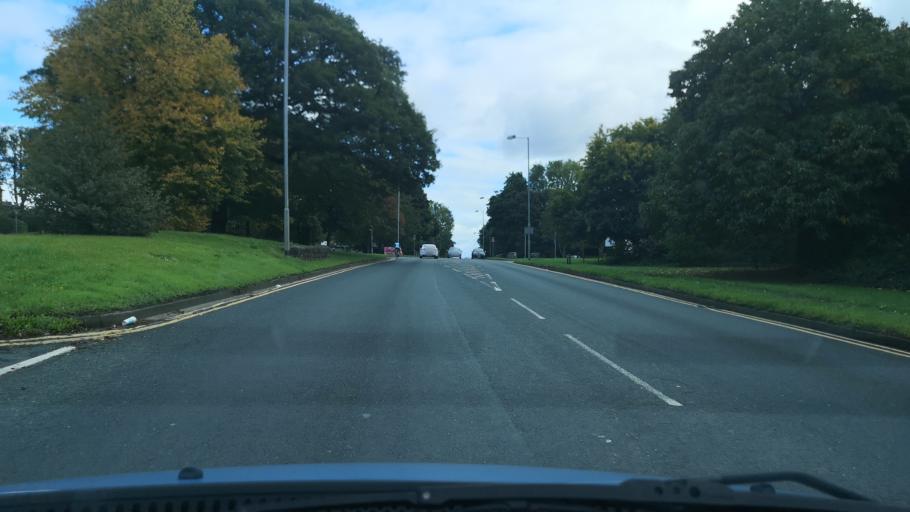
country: GB
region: England
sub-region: City and Borough of Wakefield
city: Horbury
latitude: 53.6584
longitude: -1.5637
